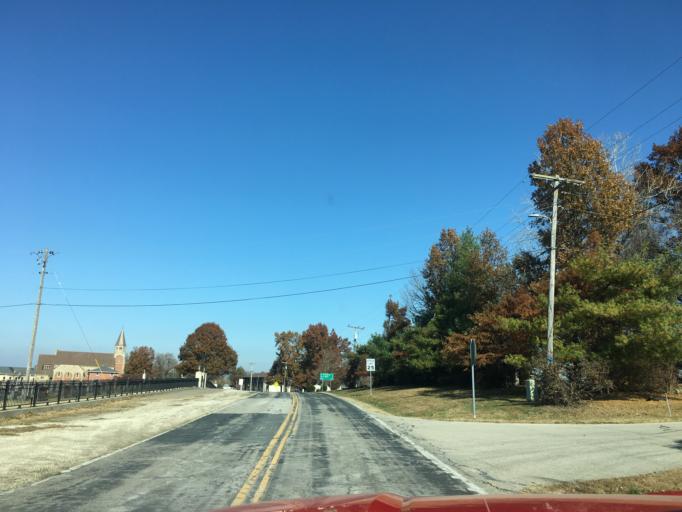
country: US
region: Missouri
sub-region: Cole County
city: Wardsville
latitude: 38.4857
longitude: -92.1757
